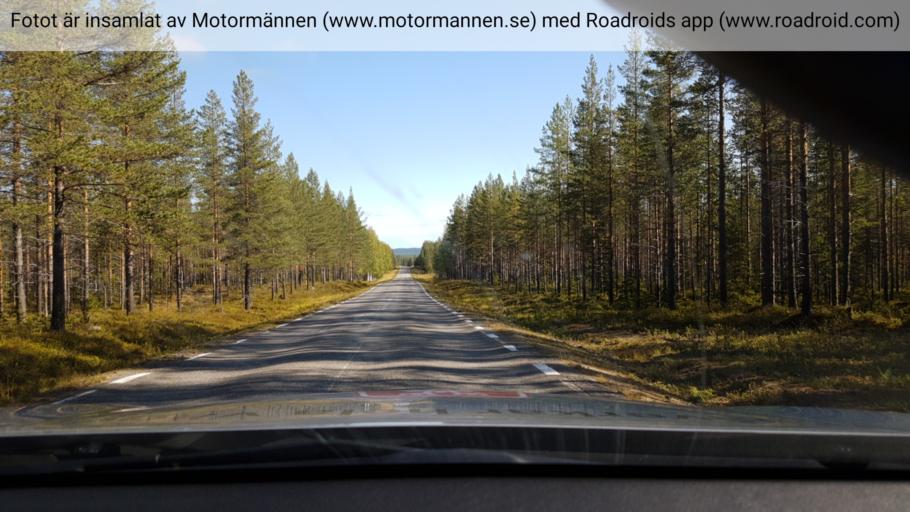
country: SE
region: Vaesterbotten
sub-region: Norsjo Kommun
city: Norsjoe
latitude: 65.1283
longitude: 19.2208
